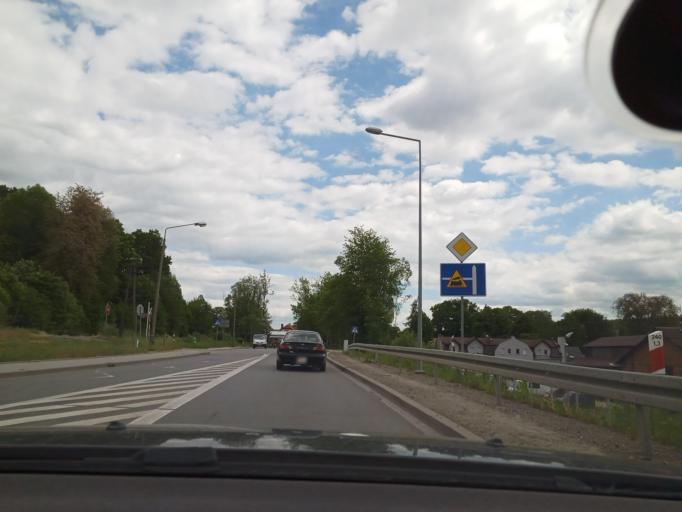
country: PL
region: Lesser Poland Voivodeship
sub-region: Powiat limanowski
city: Limanowa
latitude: 49.7258
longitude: 20.4012
